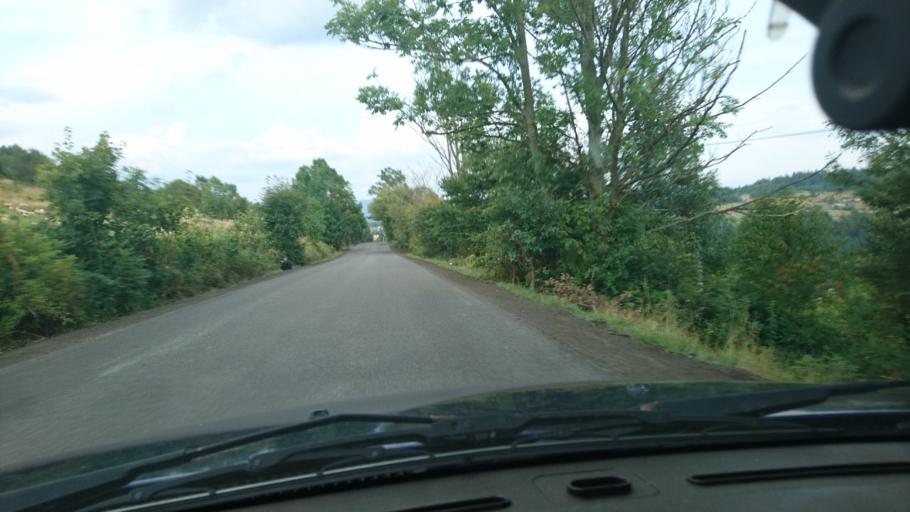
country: PL
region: Silesian Voivodeship
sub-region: Powiat zywiecki
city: Laliki
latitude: 49.5484
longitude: 19.0021
